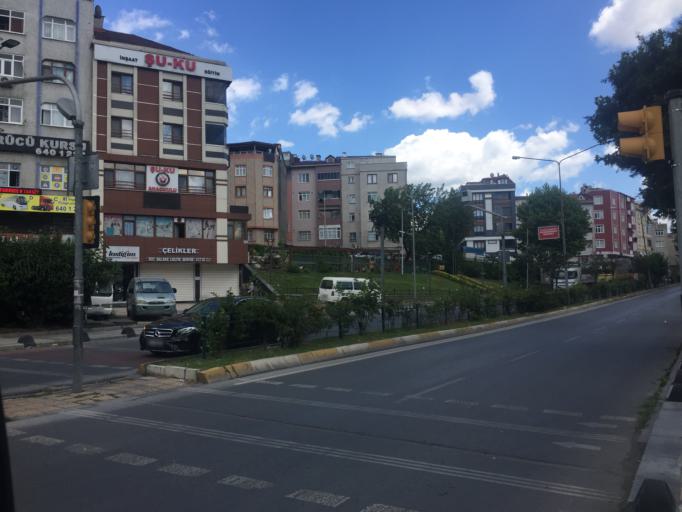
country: TR
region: Istanbul
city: Esenler
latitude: 41.0526
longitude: 28.8990
